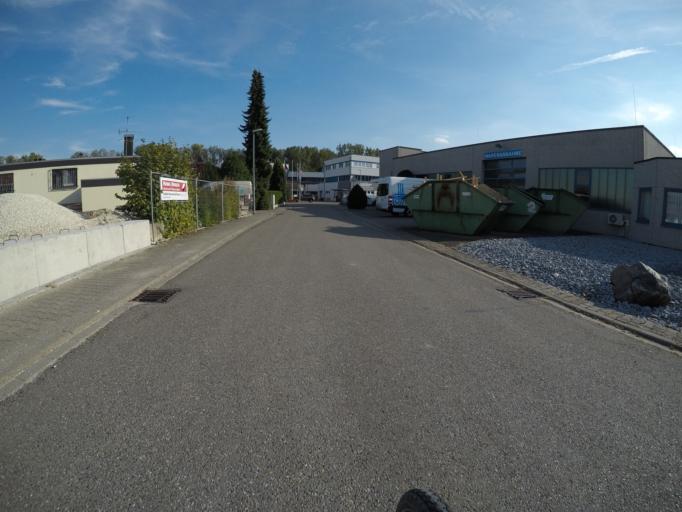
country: DE
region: Baden-Wuerttemberg
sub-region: Regierungsbezirk Stuttgart
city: Neckartailfingen
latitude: 48.6080
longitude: 9.2605
